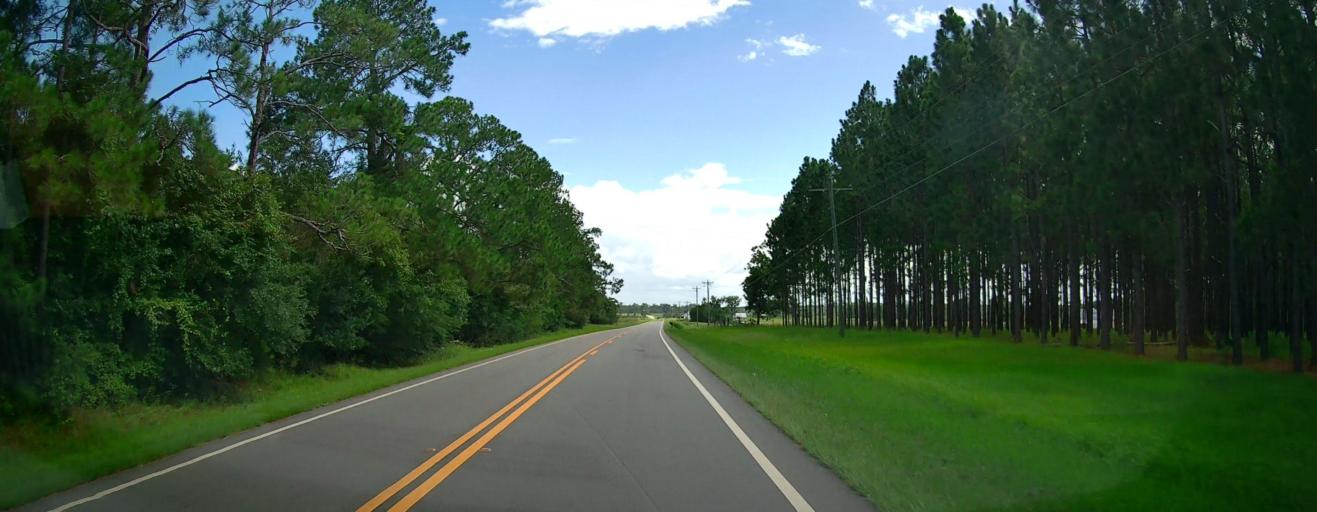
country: US
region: Georgia
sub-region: Irwin County
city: Ocilla
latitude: 31.6188
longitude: -83.1652
